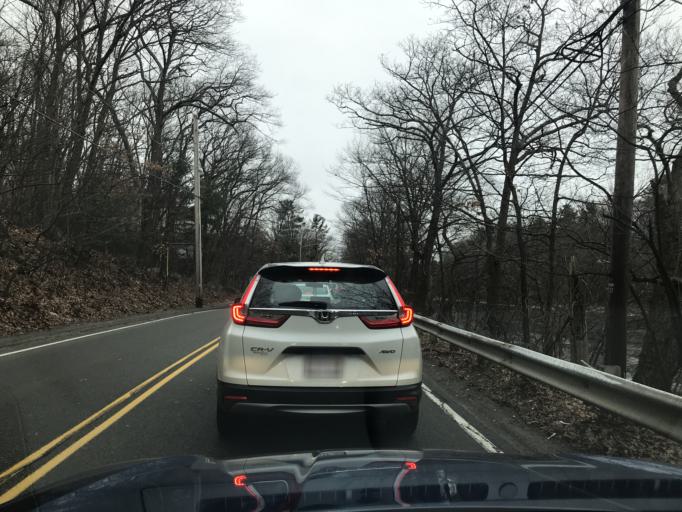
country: US
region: Massachusetts
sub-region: Essex County
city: Lynnfield
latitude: 42.5086
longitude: -71.0267
